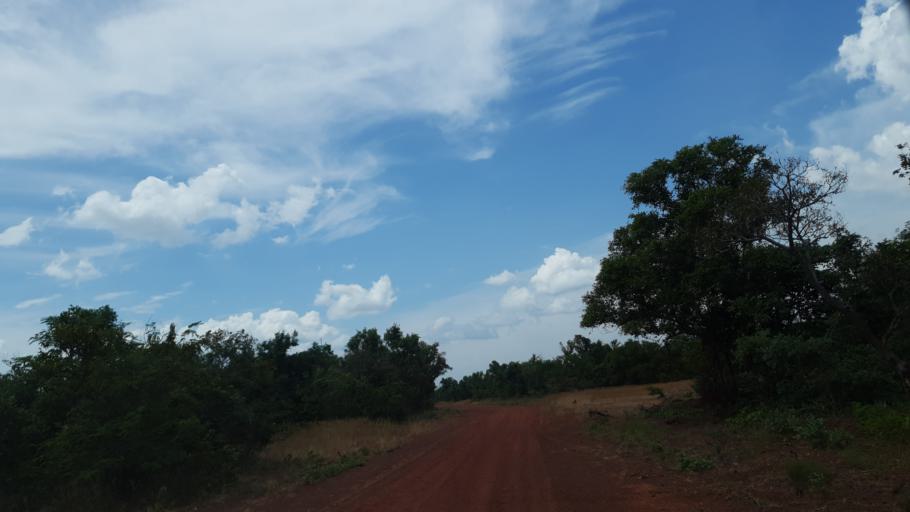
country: ML
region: Sikasso
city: Sikasso
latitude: 11.6858
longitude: -6.2081
